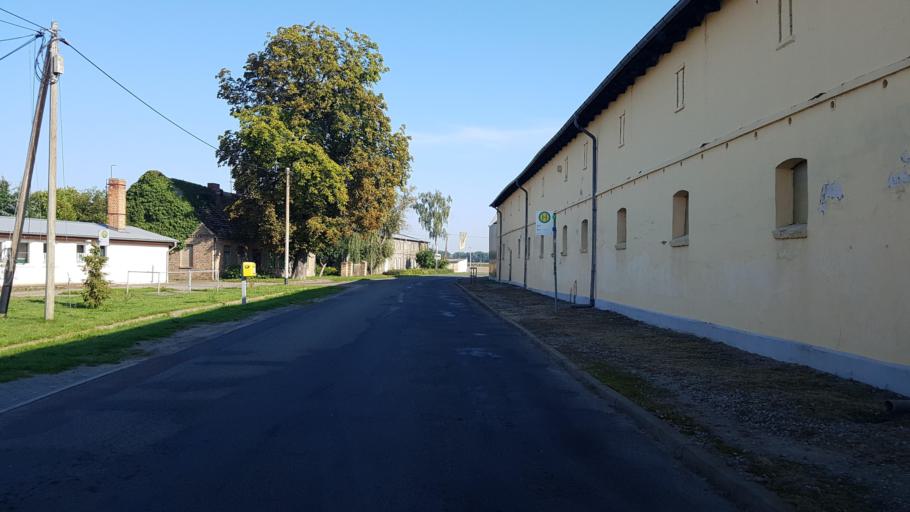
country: DE
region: Brandenburg
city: Brandenburg an der Havel
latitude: 52.4639
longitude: 12.5902
